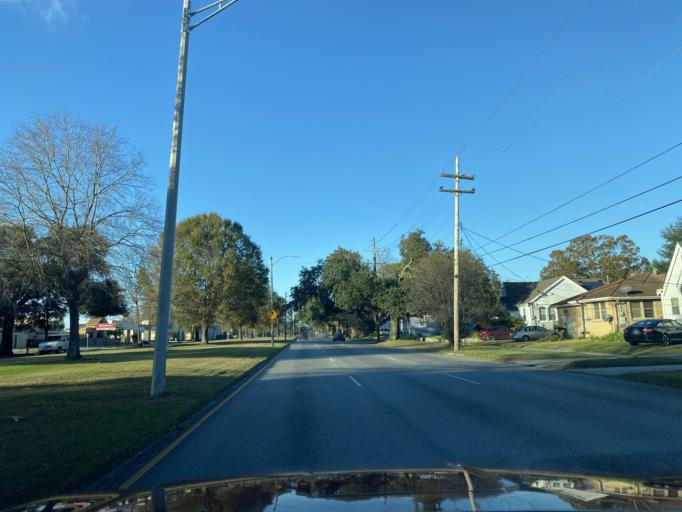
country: US
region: Louisiana
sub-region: Orleans Parish
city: New Orleans
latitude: 29.9961
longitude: -90.0589
